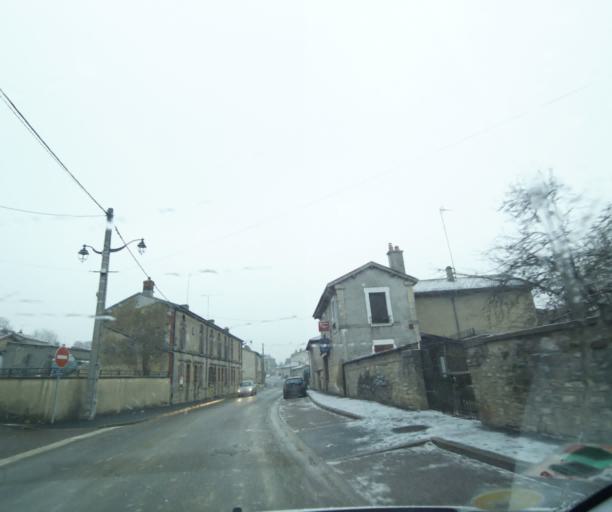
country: FR
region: Champagne-Ardenne
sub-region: Departement de la Haute-Marne
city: Wassy
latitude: 48.4928
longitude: 4.9653
